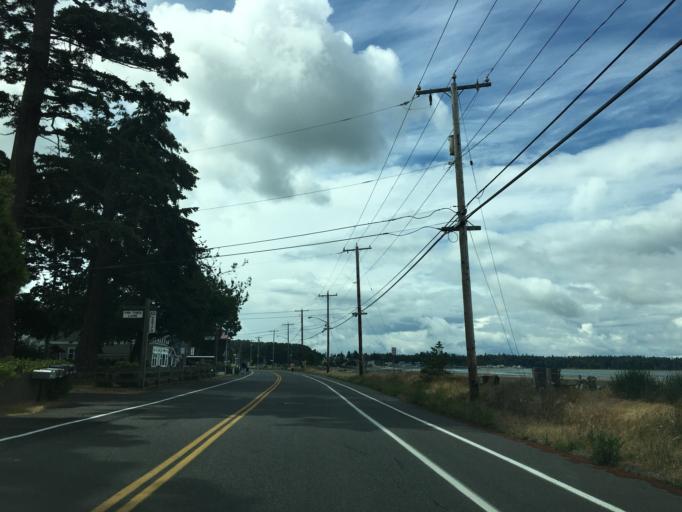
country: US
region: Washington
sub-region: Whatcom County
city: Birch Bay
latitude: 48.9243
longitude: -122.7452
